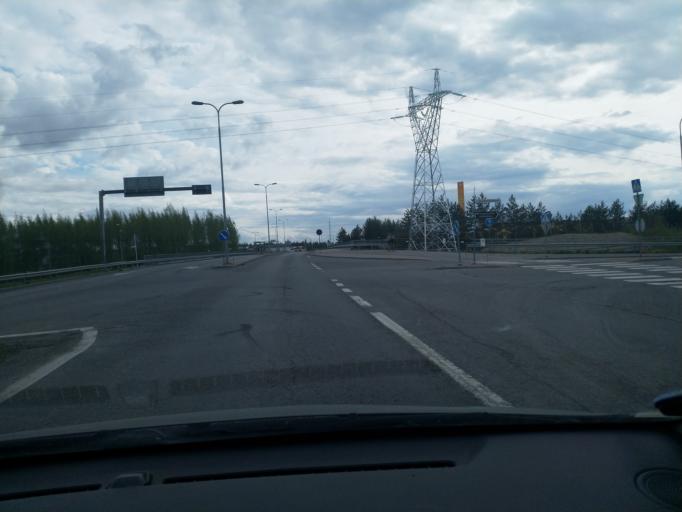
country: FI
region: Pirkanmaa
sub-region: Tampere
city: Tampere
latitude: 61.4615
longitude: 23.7921
